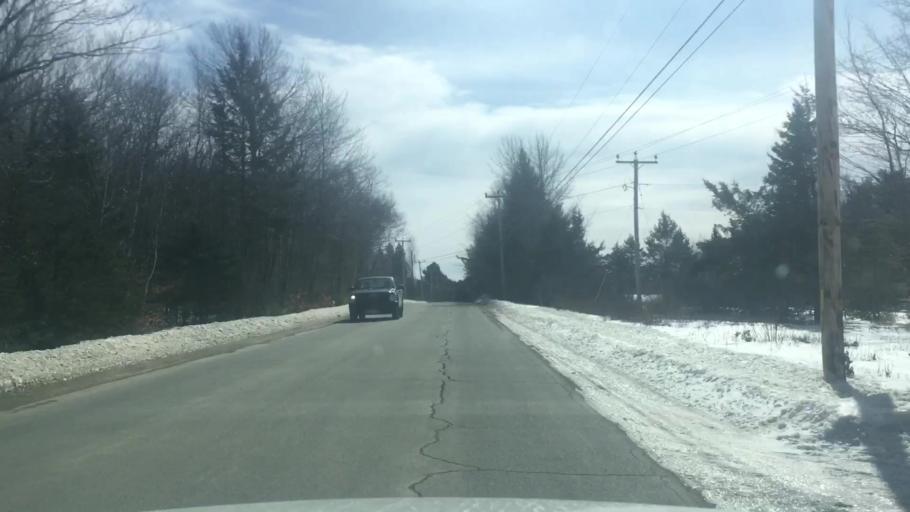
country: US
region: Maine
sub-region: Penobscot County
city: Holden
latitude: 44.7703
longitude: -68.6487
